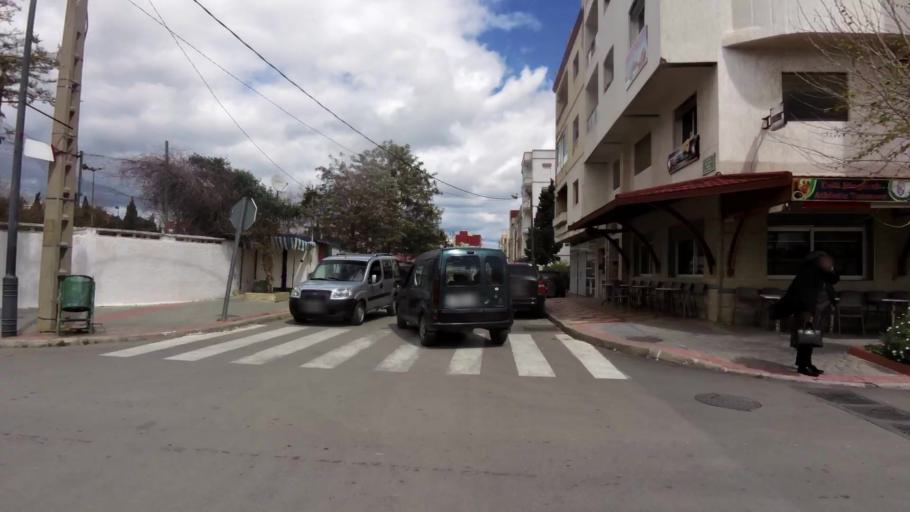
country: MA
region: Tanger-Tetouan
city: Tetouan
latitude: 35.5746
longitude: -5.3490
